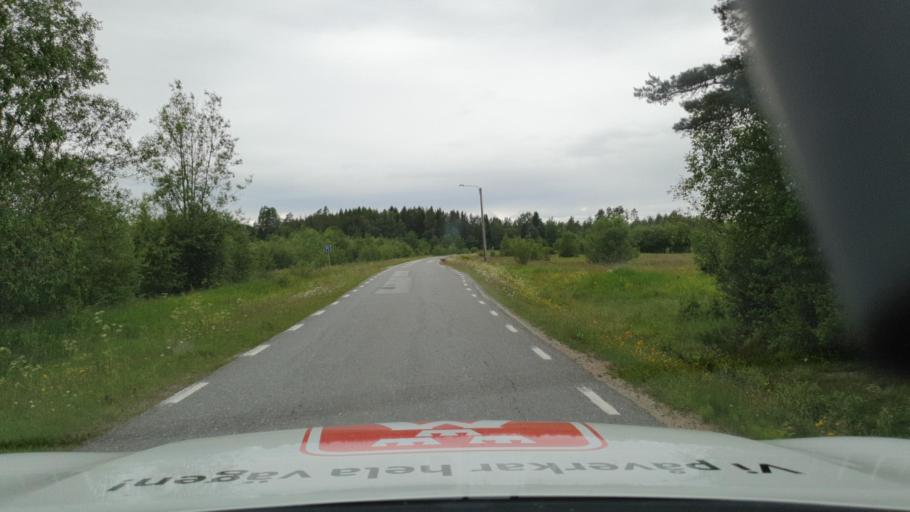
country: SE
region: Vaesterbotten
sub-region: Nordmalings Kommun
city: Nordmaling
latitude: 63.4987
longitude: 19.4239
